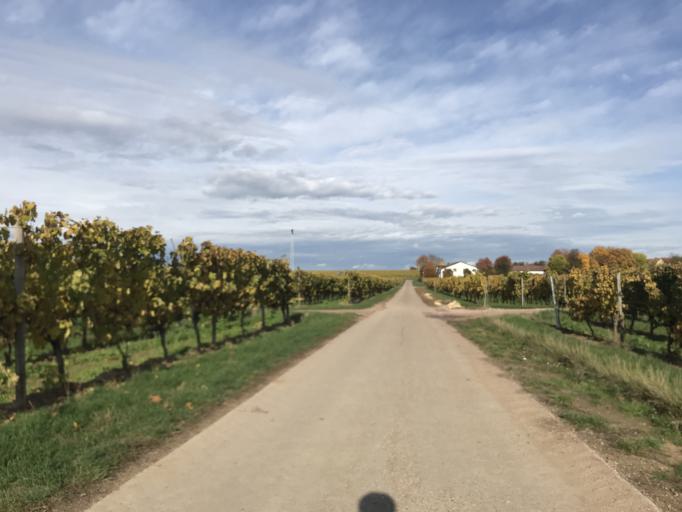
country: DE
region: Rheinland-Pfalz
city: Essenheim
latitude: 49.9242
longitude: 8.1497
